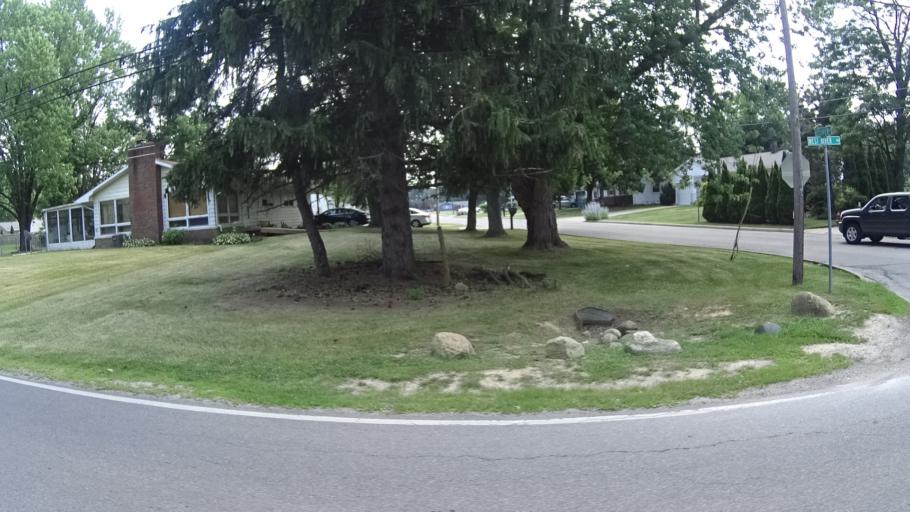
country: US
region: Ohio
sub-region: Lorain County
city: Vermilion
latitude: 41.4135
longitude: -82.3501
